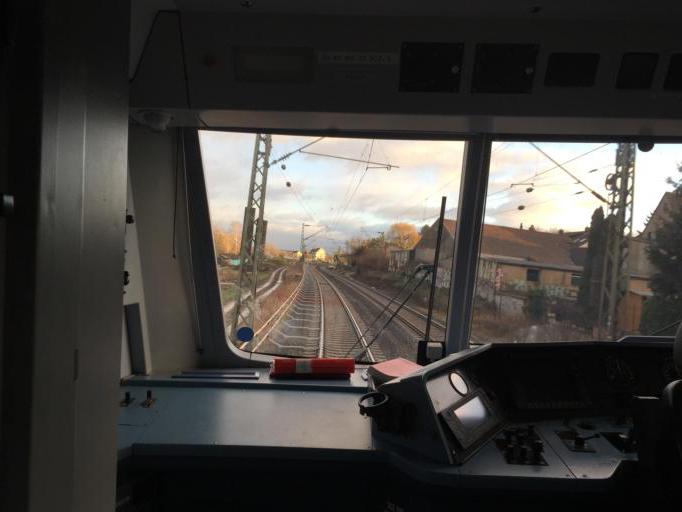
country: DE
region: Hesse
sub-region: Regierungsbezirk Darmstadt
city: Bad Vilbel
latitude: 50.1736
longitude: 8.6948
